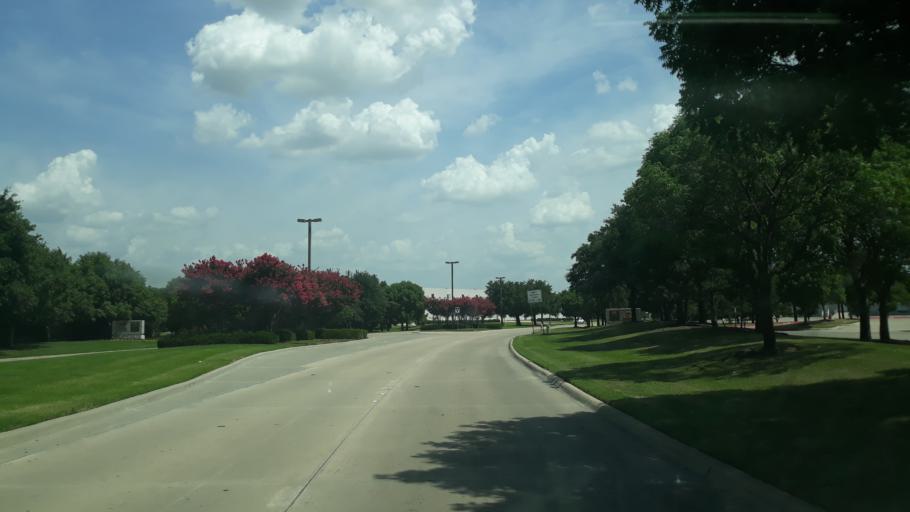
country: US
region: Texas
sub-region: Dallas County
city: Coppell
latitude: 32.9579
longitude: -97.0117
